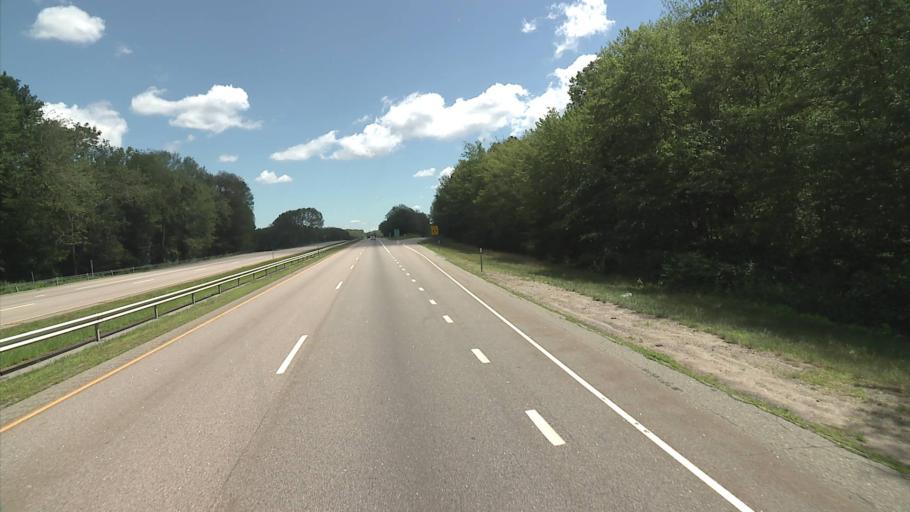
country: US
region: Connecticut
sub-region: New London County
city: Central Waterford
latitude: 41.3937
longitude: -72.1704
